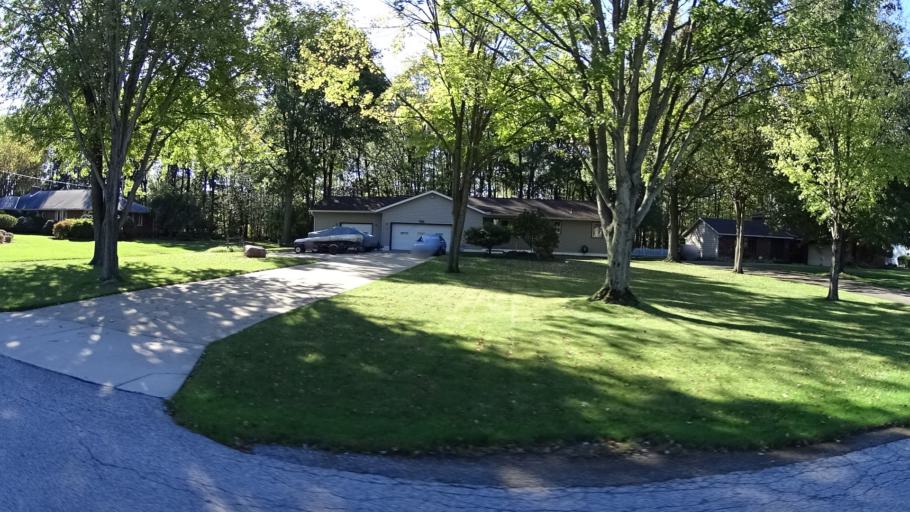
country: US
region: Ohio
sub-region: Lorain County
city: Amherst
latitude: 41.4150
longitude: -82.2141
